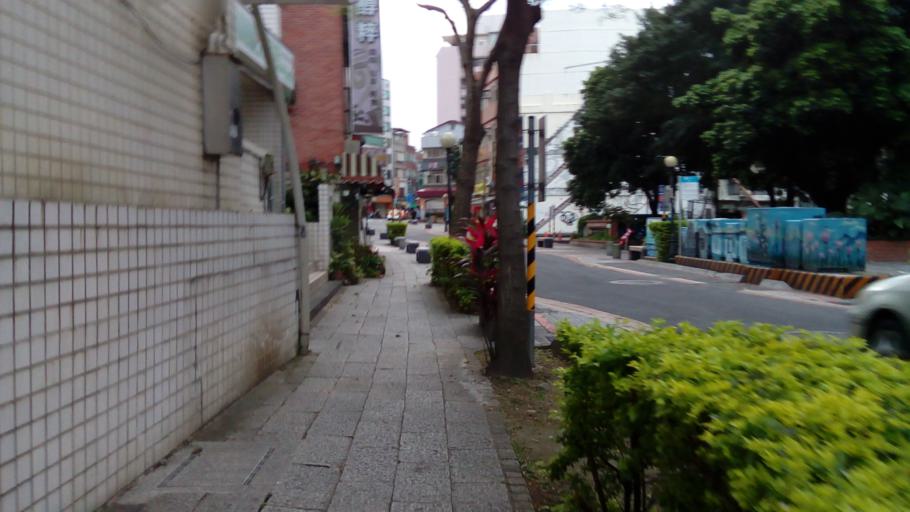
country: TW
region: Taipei
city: Taipei
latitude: 25.1719
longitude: 121.4377
